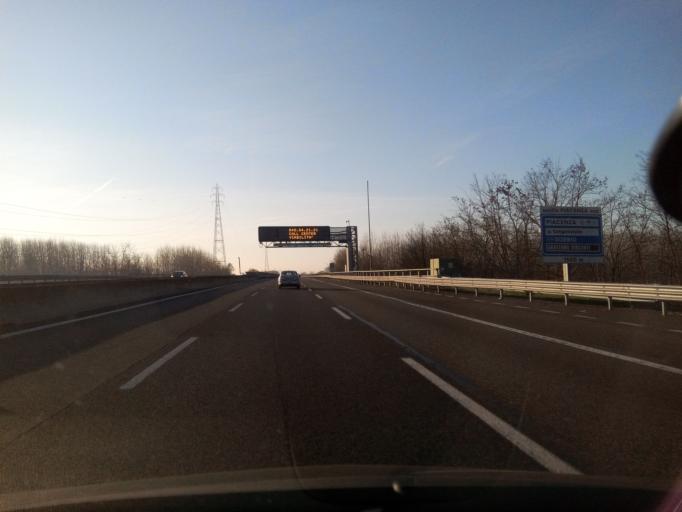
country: IT
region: Lombardy
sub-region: Provincia di Lodi
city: San Rocco al Porto
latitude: 45.0721
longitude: 9.7279
